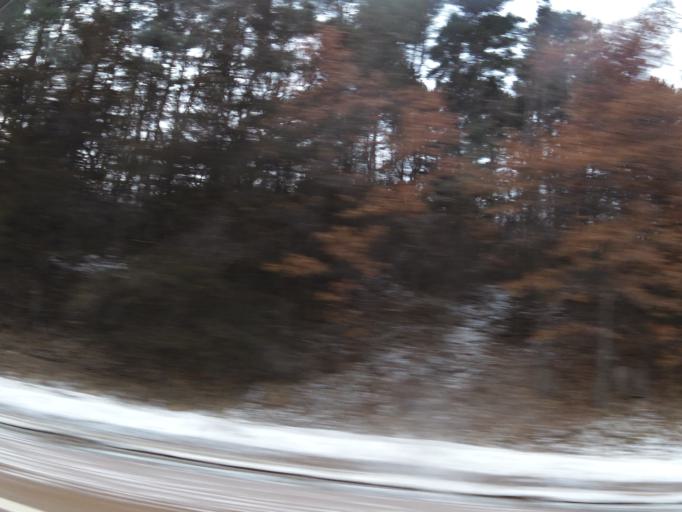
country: US
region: Minnesota
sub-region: Carver County
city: Carver
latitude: 44.7477
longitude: -93.6528
